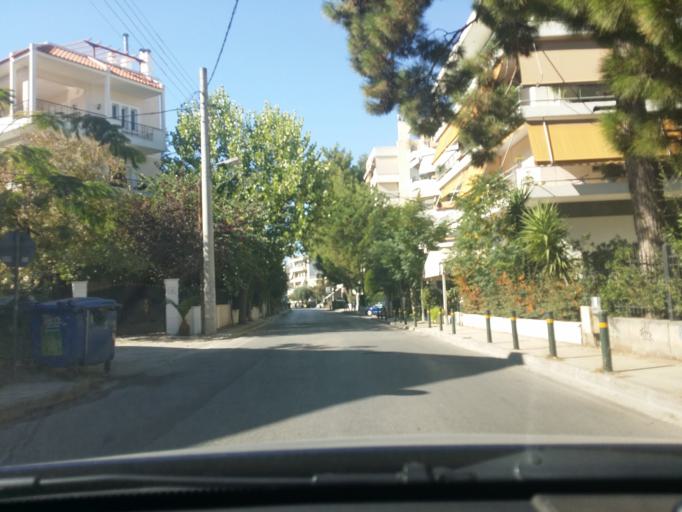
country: GR
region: Attica
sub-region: Nomarchia Athinas
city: Agia Paraskevi
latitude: 38.0159
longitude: 23.8356
